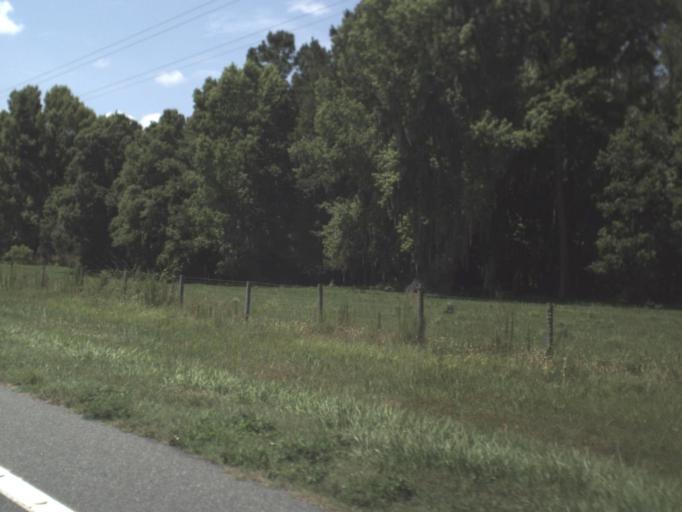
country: US
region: Florida
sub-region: Levy County
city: Williston
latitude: 29.4621
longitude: -82.4140
